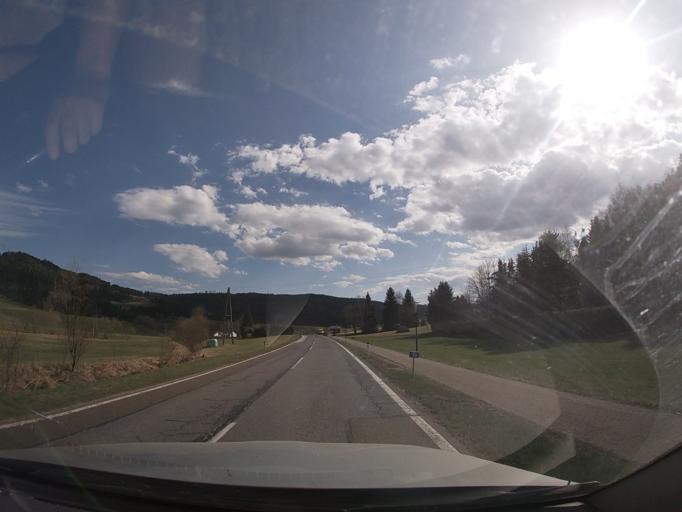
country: AT
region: Styria
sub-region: Politischer Bezirk Murau
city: Perchau am Sattel
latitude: 47.1046
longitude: 14.4564
